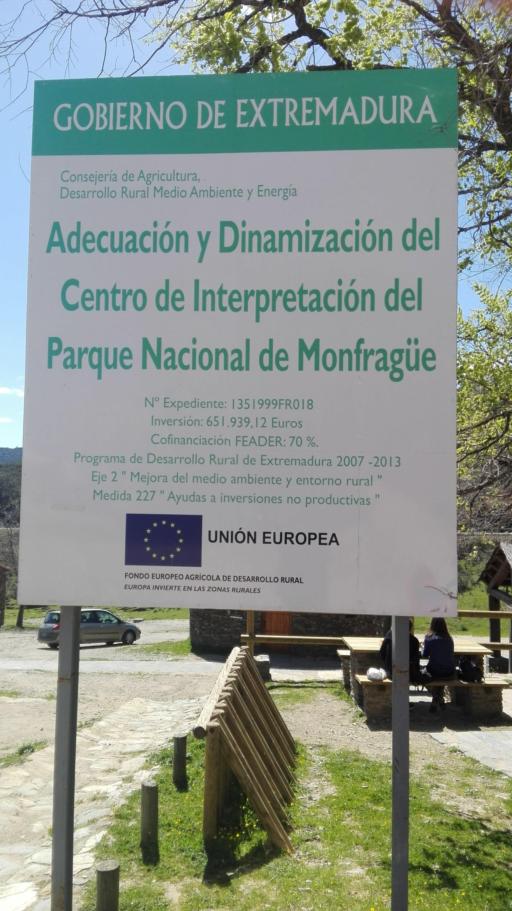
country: ES
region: Extremadura
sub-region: Provincia de Caceres
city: Torrejon el Rubio
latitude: 39.8469
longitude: -6.0291
